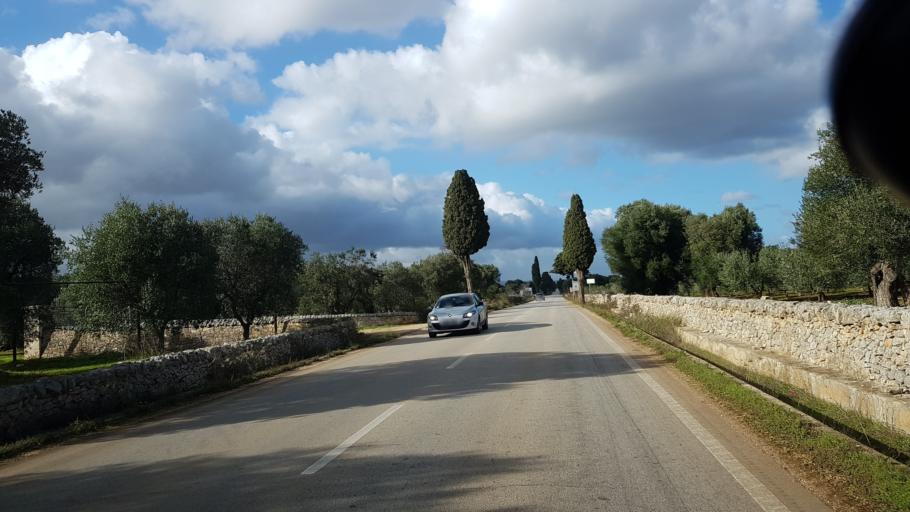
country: IT
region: Apulia
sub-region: Provincia di Brindisi
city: Montalbano
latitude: 40.7720
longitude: 17.5034
